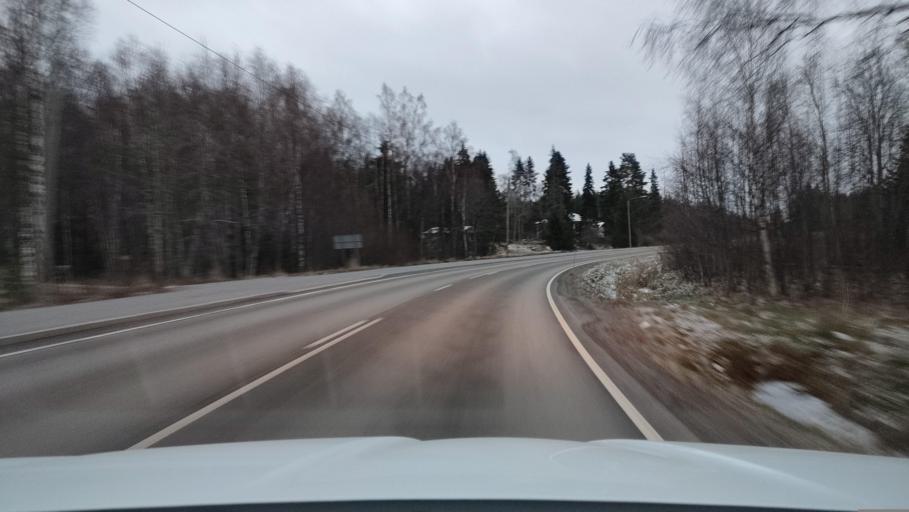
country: FI
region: Ostrobothnia
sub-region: Vaasa
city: Replot
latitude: 63.2184
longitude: 21.4236
